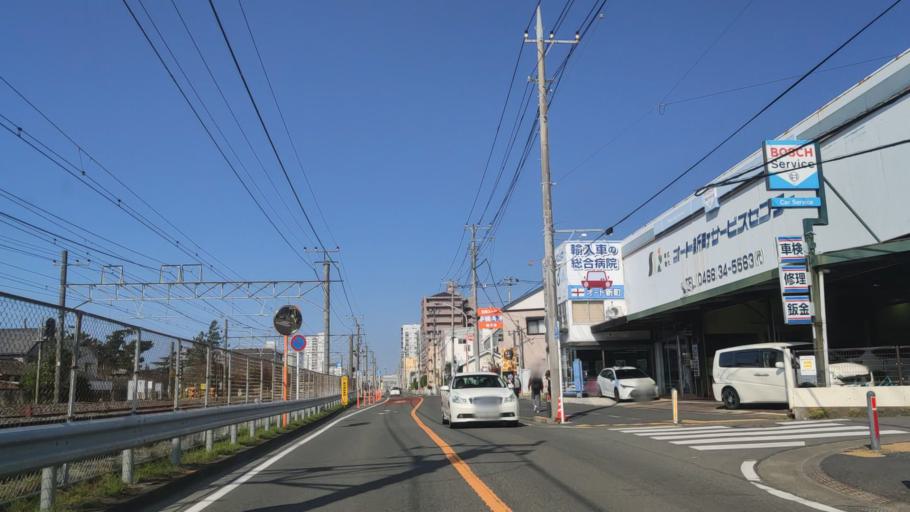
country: JP
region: Kanagawa
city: Fujisawa
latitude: 35.3375
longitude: 139.4576
